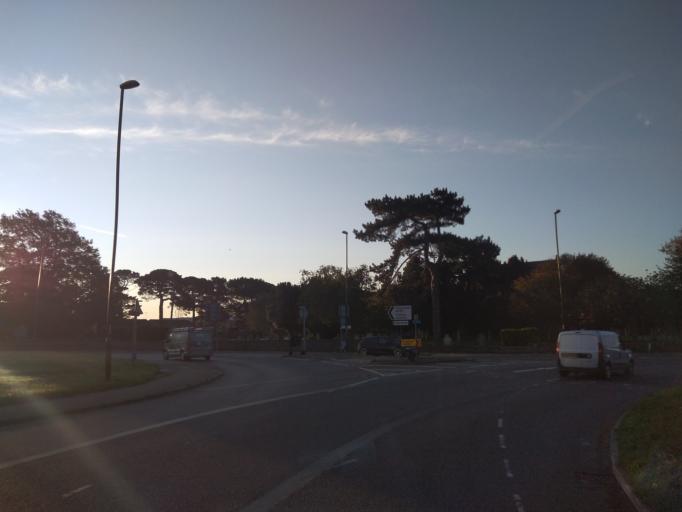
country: GB
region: England
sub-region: West Sussex
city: Littlehampton
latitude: 50.8202
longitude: -0.5280
